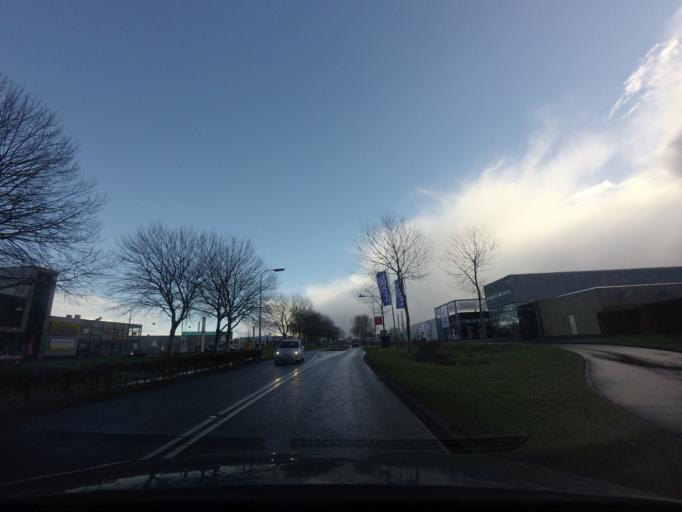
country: NL
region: Groningen
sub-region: Gemeente Groningen
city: Groningen
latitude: 53.2142
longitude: 6.5339
